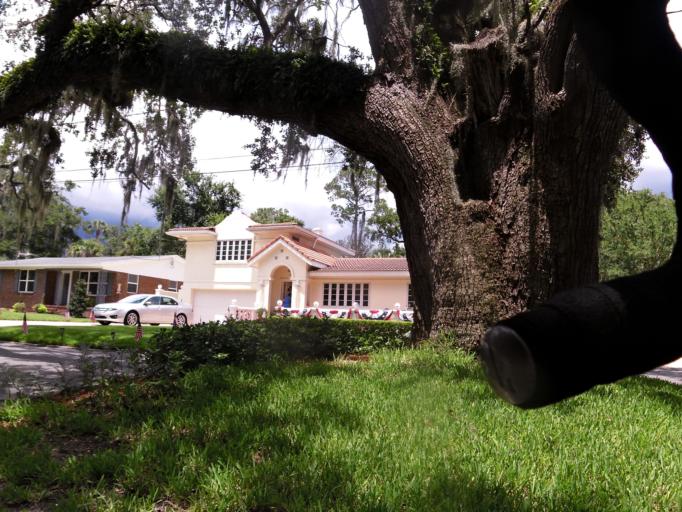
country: US
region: Florida
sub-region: Duval County
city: Jacksonville
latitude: 30.3006
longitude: -81.6967
